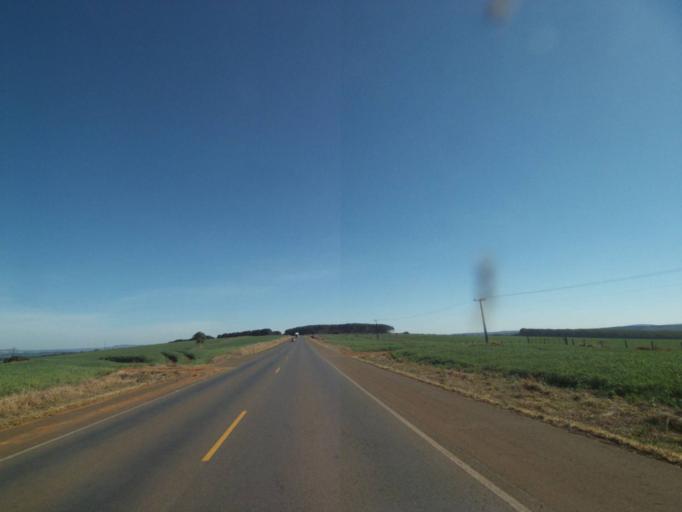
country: BR
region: Parana
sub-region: Tibagi
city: Tibagi
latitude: -24.4296
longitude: -50.4061
